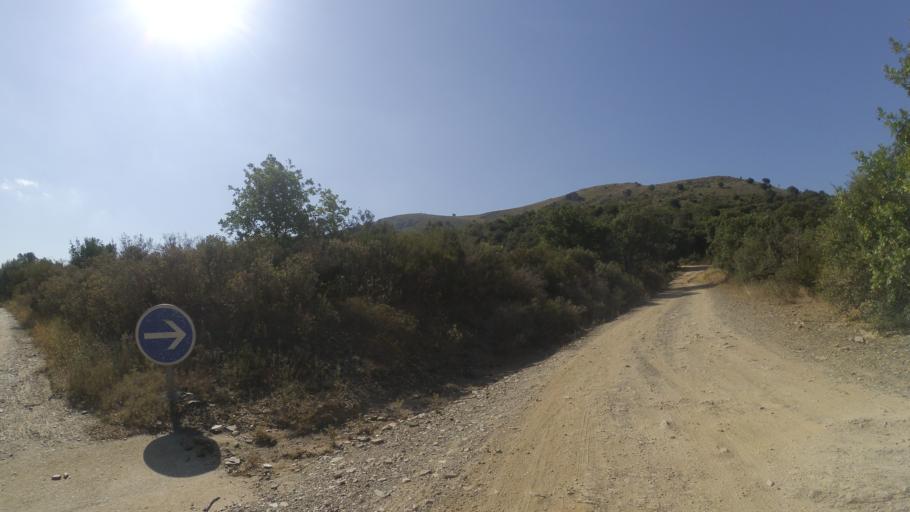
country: FR
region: Languedoc-Roussillon
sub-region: Departement des Pyrenees-Orientales
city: Millas
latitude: 42.6293
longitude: 2.6778
